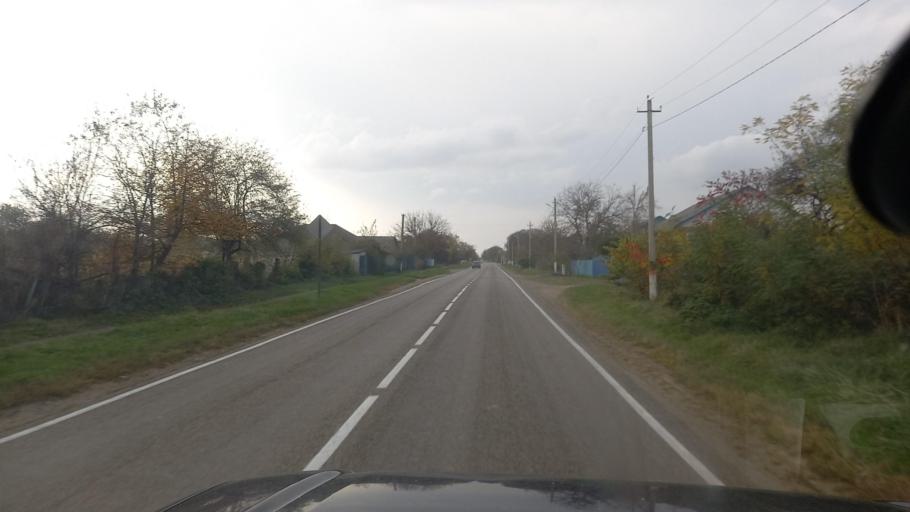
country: RU
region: Krasnodarskiy
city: Gubskaya
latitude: 44.3177
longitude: 40.6239
